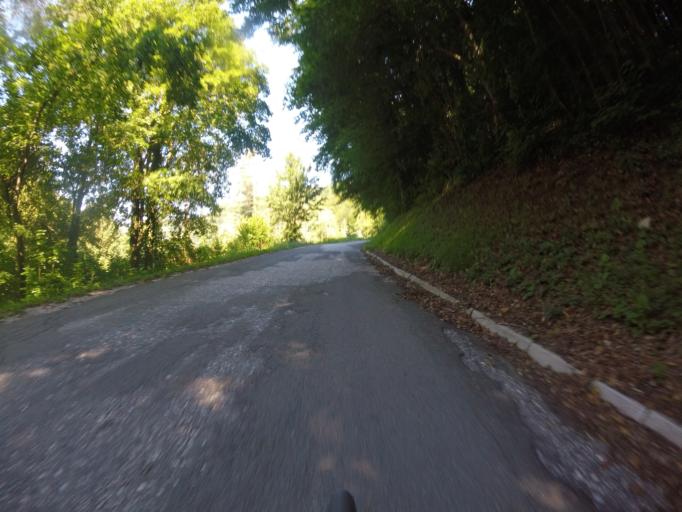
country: SI
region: Brezice
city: Brezice
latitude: 45.8368
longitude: 15.6077
